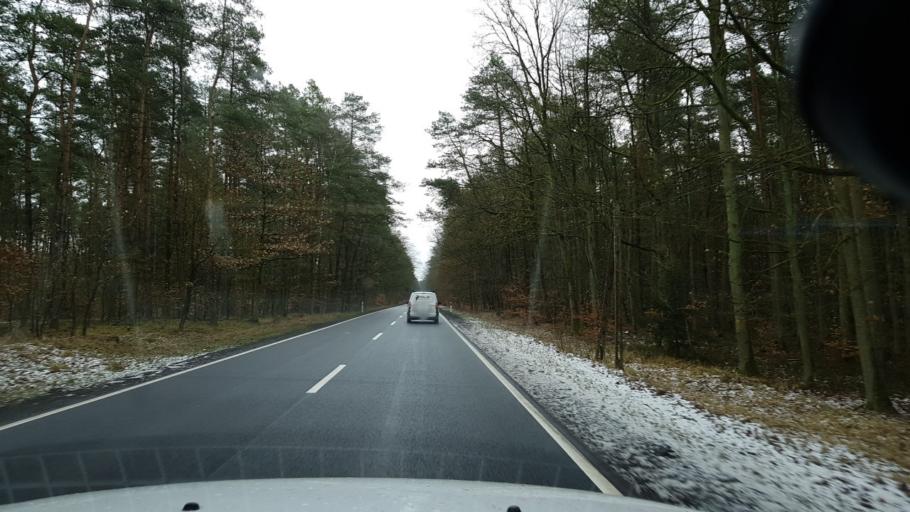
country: PL
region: West Pomeranian Voivodeship
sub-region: Powiat goleniowski
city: Stepnica
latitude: 53.6291
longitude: 14.6754
